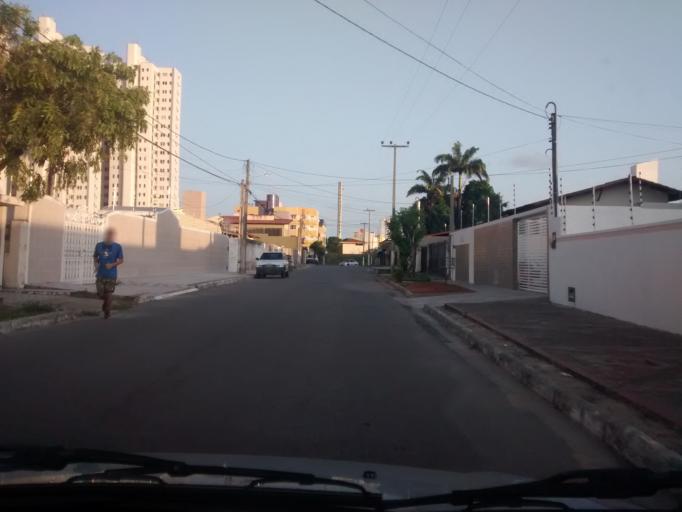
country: BR
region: Rio Grande do Norte
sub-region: Natal
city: Natal
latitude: -5.8669
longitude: -35.1880
